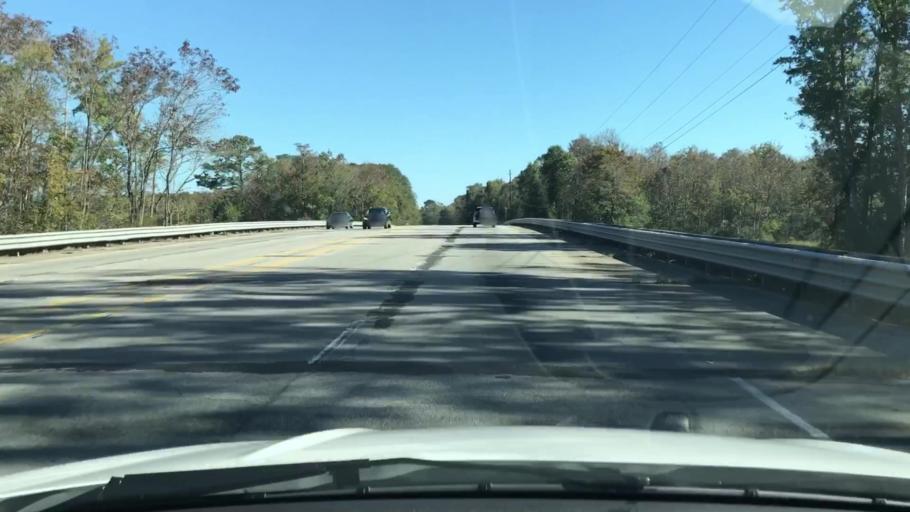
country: US
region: South Carolina
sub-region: Charleston County
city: Ravenel
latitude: 32.7653
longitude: -80.4473
